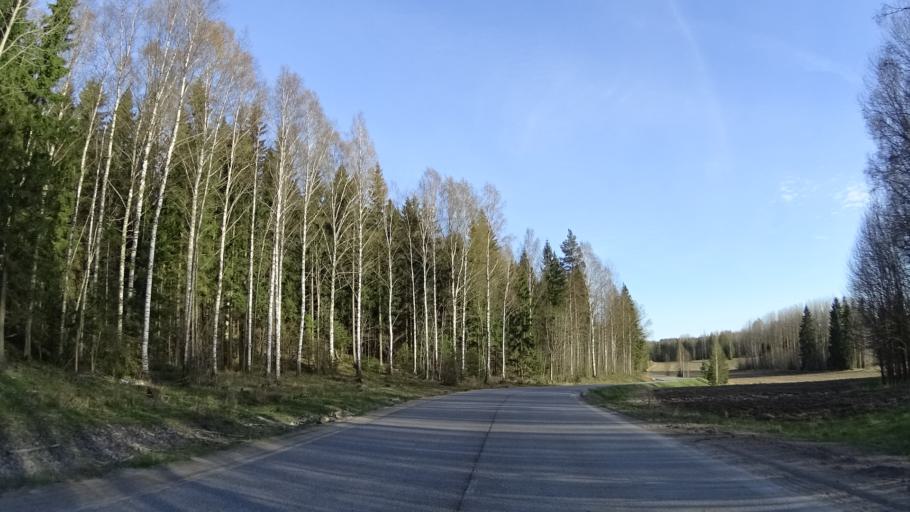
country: FI
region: Uusimaa
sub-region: Helsinki
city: Kilo
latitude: 60.3000
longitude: 24.7958
